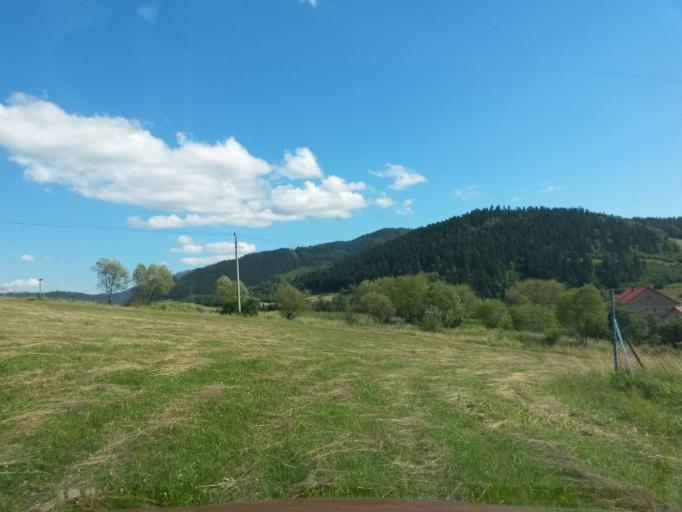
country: SK
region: Kosicky
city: Spisska Nova Ves
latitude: 48.8444
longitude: 20.6217
